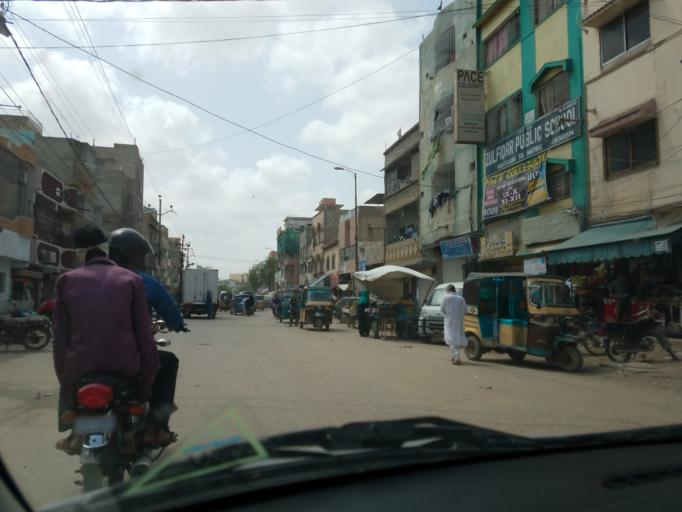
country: PK
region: Sindh
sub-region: Karachi District
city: Karachi
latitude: 24.9480
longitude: 67.0793
